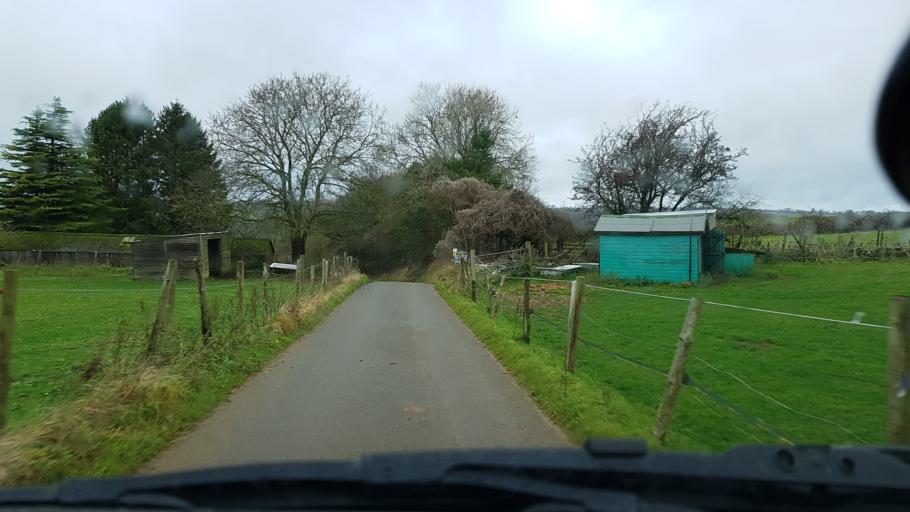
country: GB
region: England
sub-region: Gloucestershire
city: Charlton Kings
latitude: 51.8477
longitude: -2.0392
